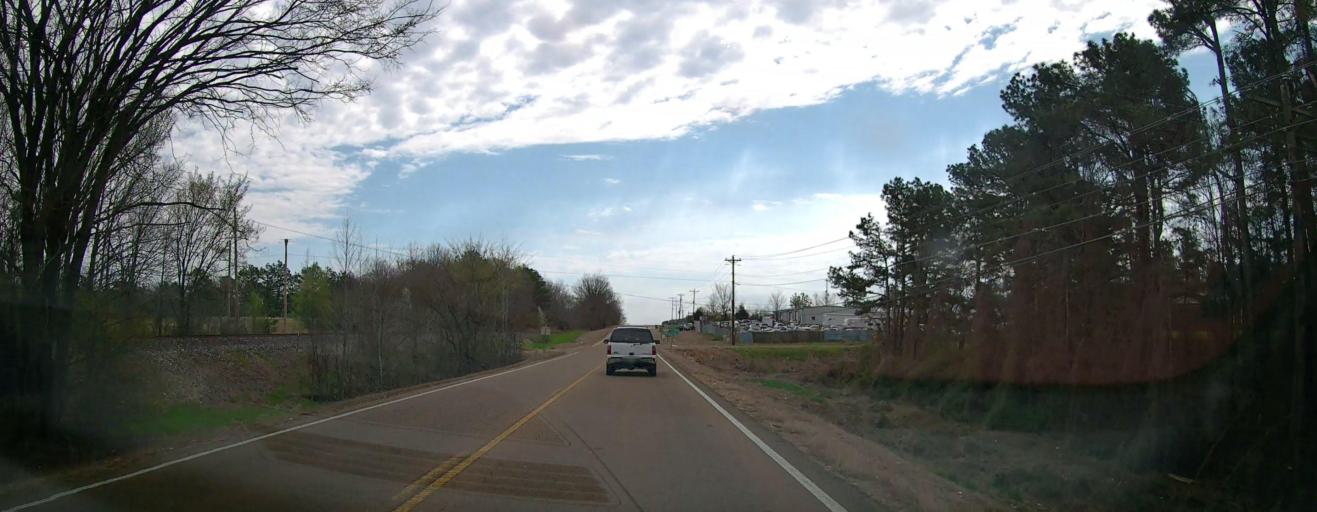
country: US
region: Mississippi
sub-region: Marshall County
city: Byhalia
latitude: 34.8865
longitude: -89.7247
